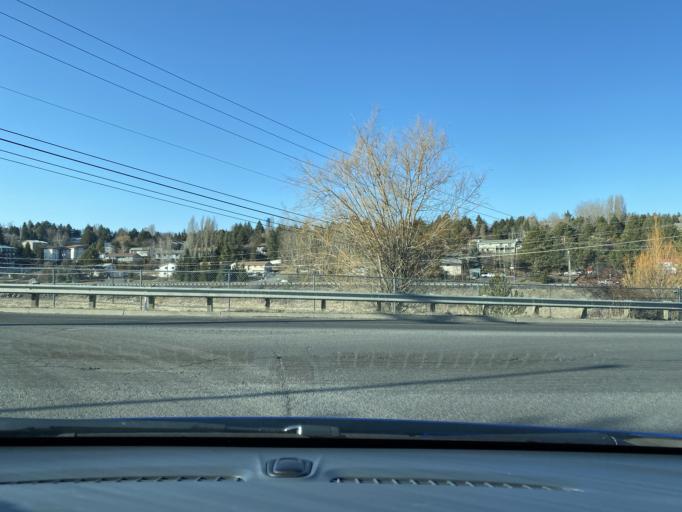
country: US
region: Washington
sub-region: Whitman County
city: Pullman
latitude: 46.7497
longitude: -117.1698
